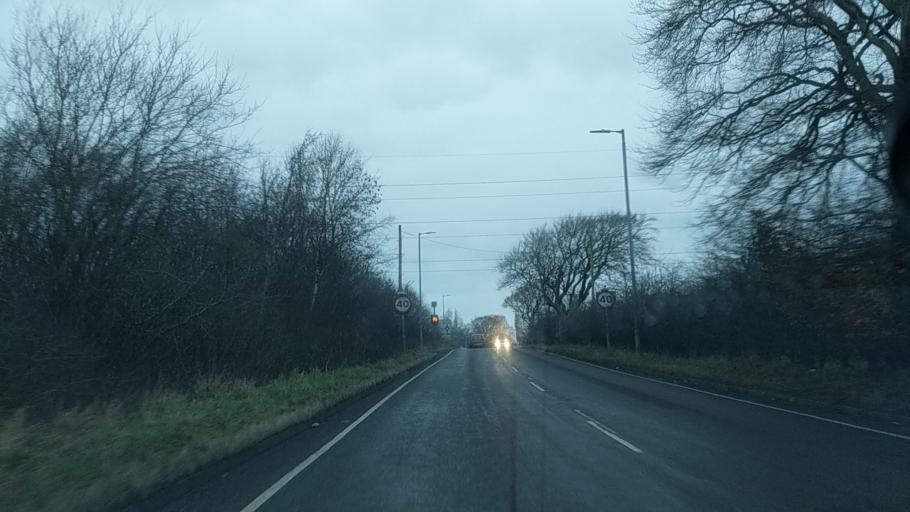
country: GB
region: Scotland
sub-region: South Lanarkshire
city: East Kilbride
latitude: 55.7412
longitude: -4.1576
